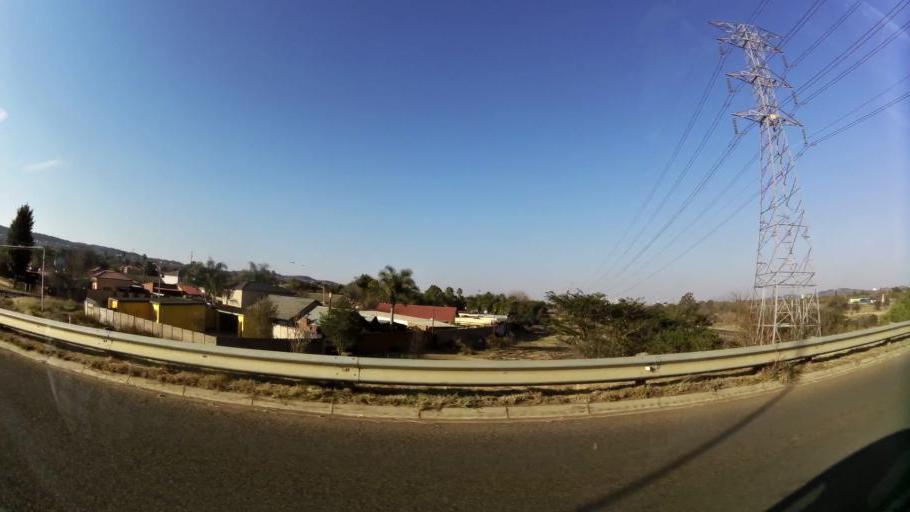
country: ZA
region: Gauteng
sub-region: City of Tshwane Metropolitan Municipality
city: Pretoria
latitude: -25.7479
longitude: 28.1186
